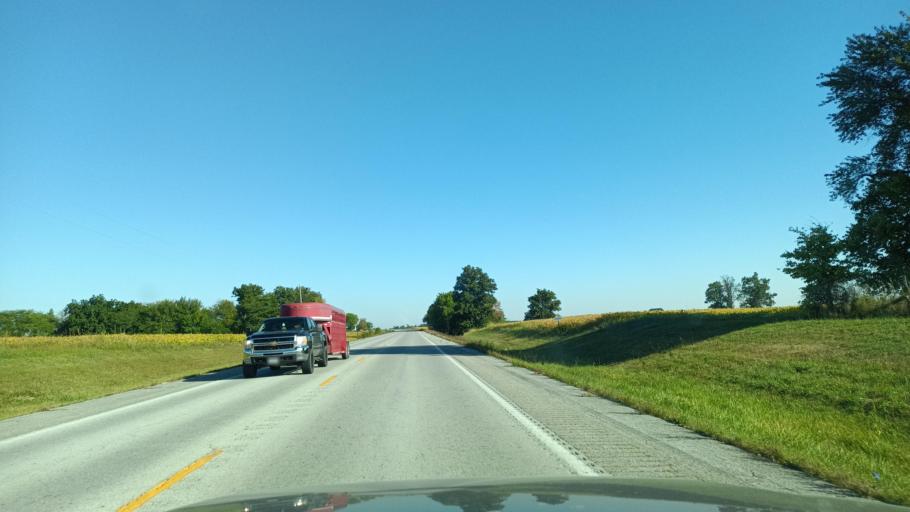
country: US
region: Missouri
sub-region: Audrain County
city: Vandalia
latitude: 39.3136
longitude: -91.6433
